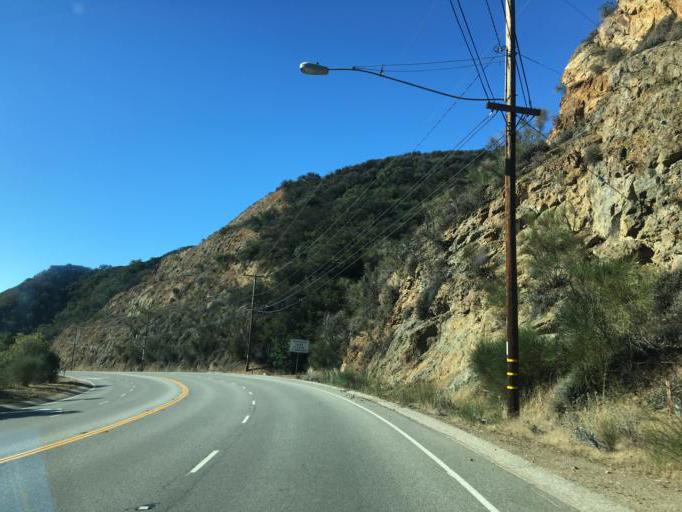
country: US
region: California
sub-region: Los Angeles County
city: Malibu
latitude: 34.0695
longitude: -118.8121
